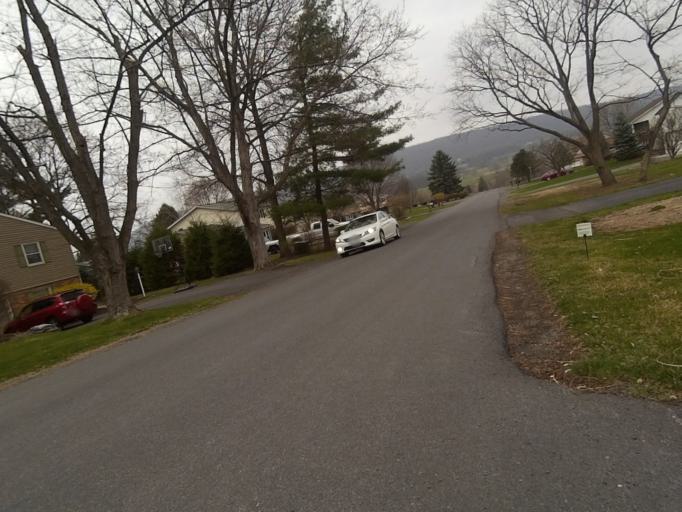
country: US
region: Pennsylvania
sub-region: Centre County
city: Boalsburg
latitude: 40.7870
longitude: -77.7761
